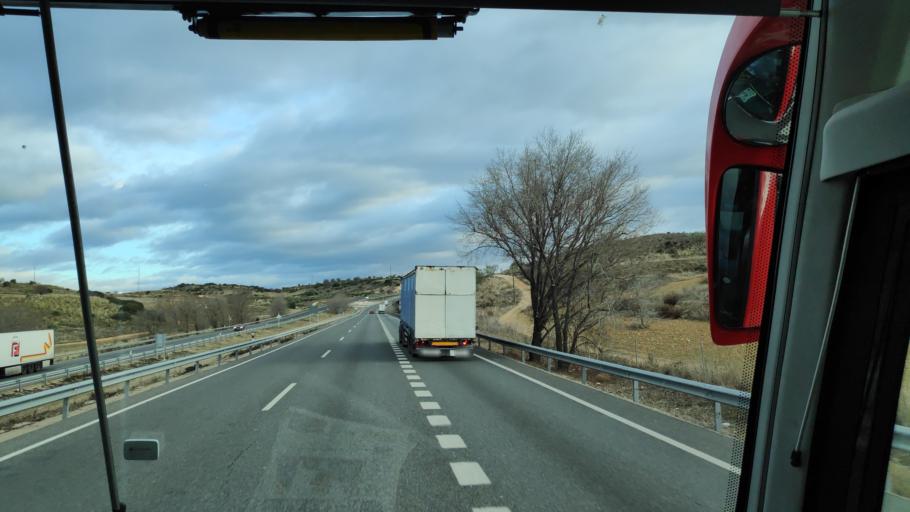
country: ES
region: Madrid
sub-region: Provincia de Madrid
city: Villarejo de Salvanes
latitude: 40.1966
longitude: -3.3068
